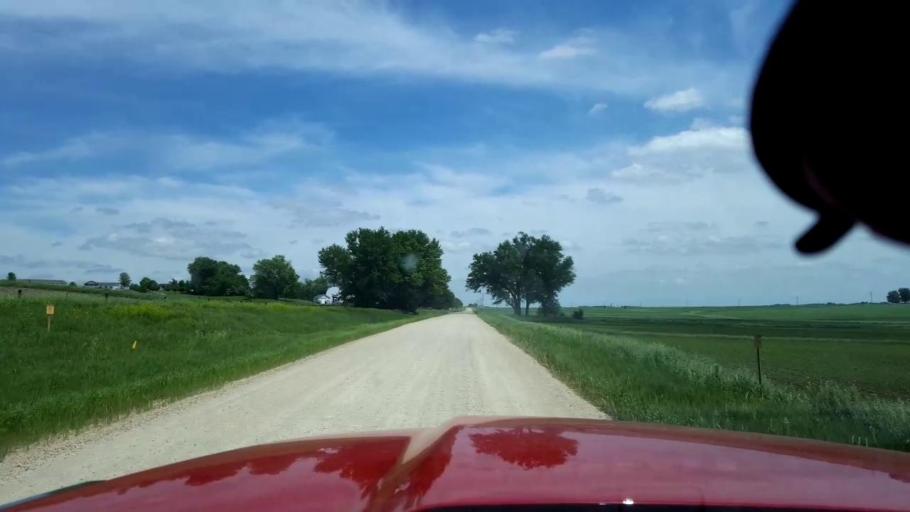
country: US
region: Iowa
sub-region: Linn County
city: Lisbon
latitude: 41.9553
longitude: -91.3628
